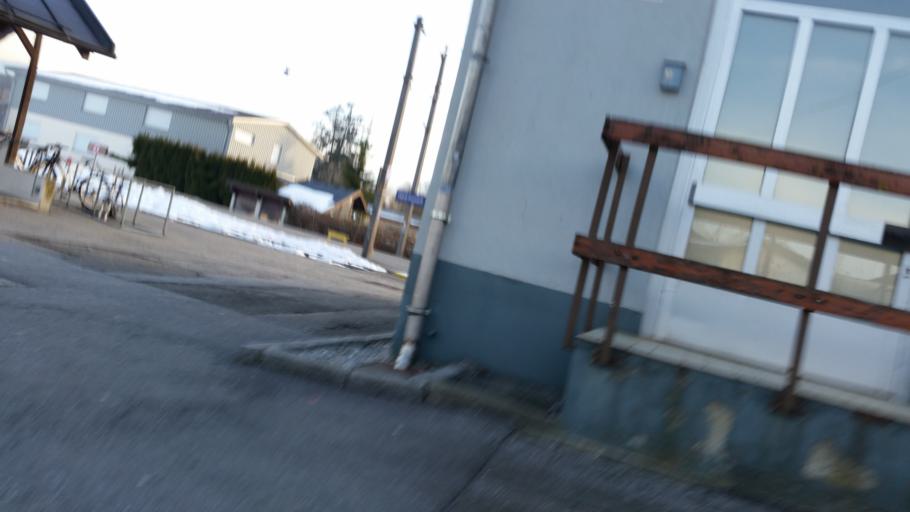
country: AT
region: Vorarlberg
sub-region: Politischer Bezirk Bregenz
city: Hard
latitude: 47.4801
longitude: 9.6882
